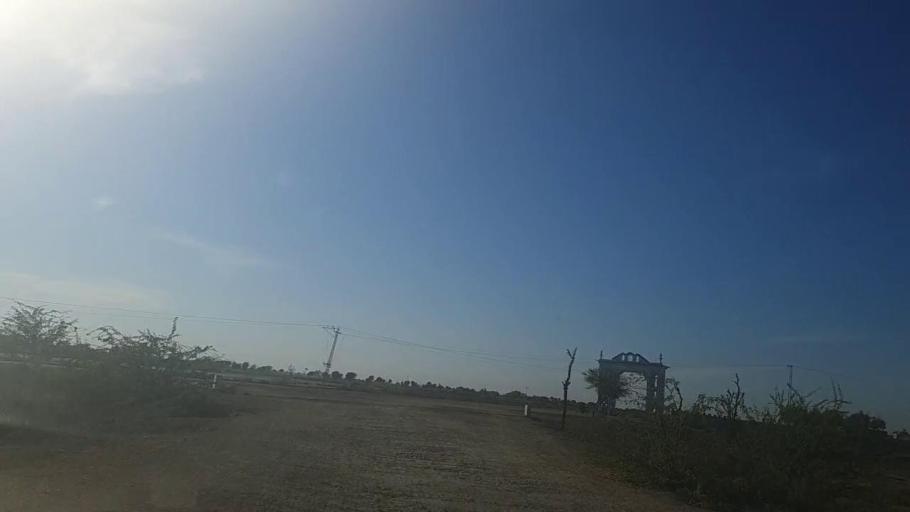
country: PK
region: Sindh
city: Pithoro
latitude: 25.5229
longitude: 69.3728
